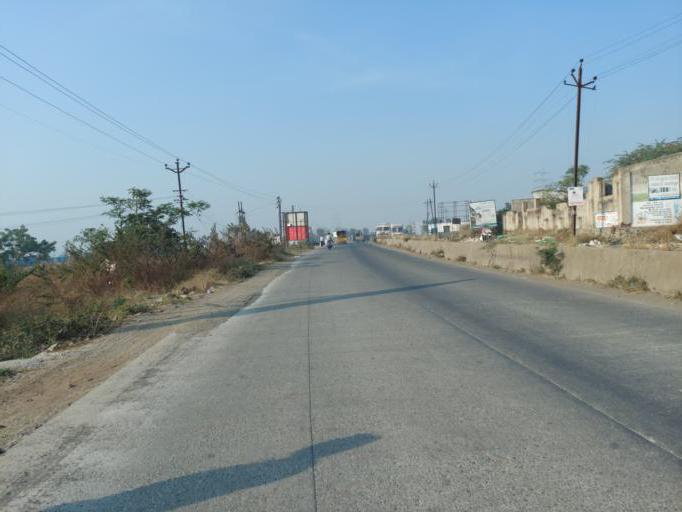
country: IN
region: Maharashtra
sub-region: Pune Division
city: Pune
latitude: 18.4577
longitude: 73.9466
